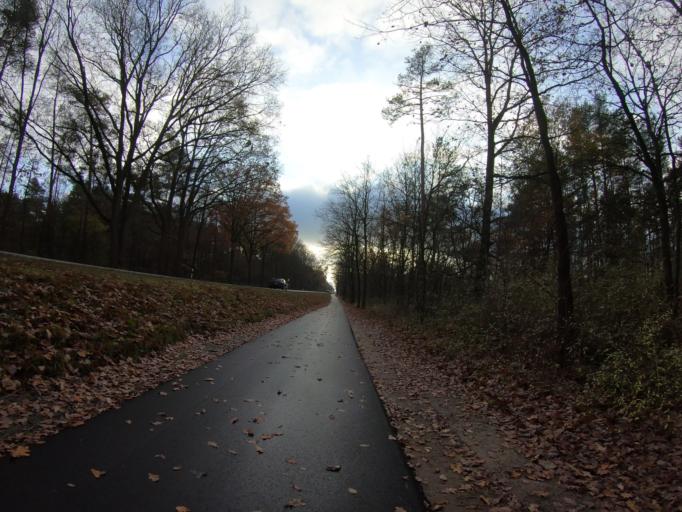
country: DE
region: Lower Saxony
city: Wesendorf
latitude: 52.5770
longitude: 10.5252
